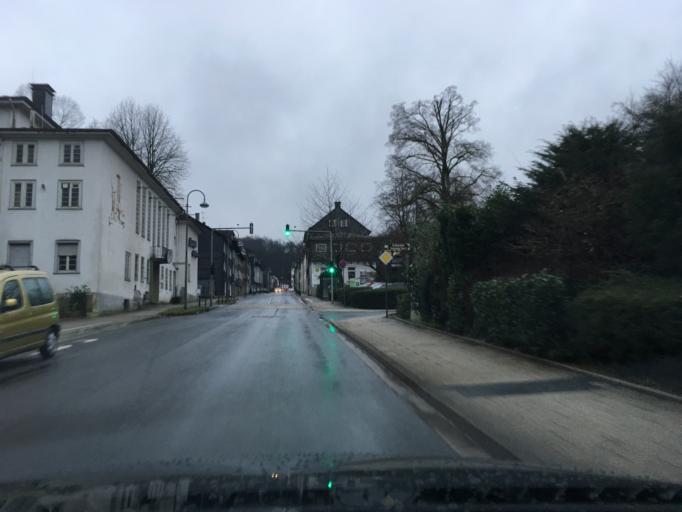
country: DE
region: North Rhine-Westphalia
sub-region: Regierungsbezirk Dusseldorf
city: Velbert
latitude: 51.3110
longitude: 7.0860
